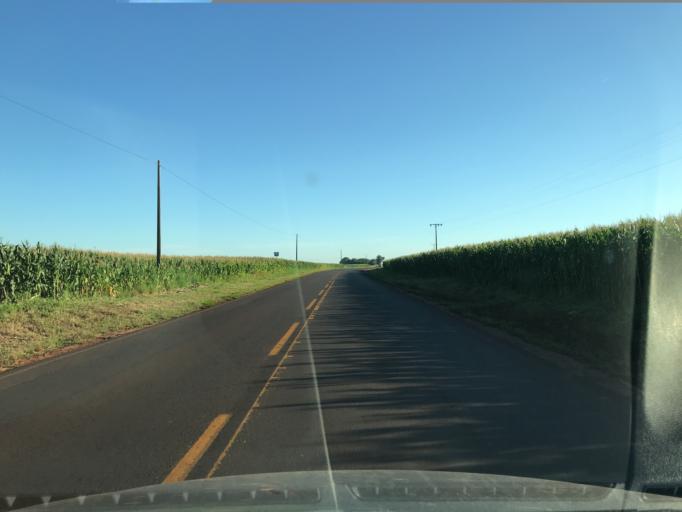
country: BR
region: Parana
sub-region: Palotina
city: Palotina
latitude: -24.1174
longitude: -53.8475
